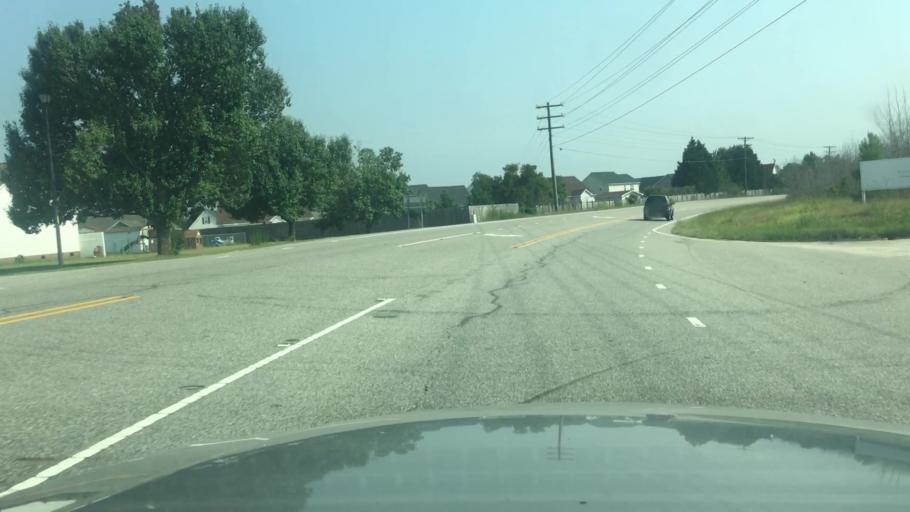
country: US
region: North Carolina
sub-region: Cumberland County
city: Hope Mills
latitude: 34.9193
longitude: -78.9106
